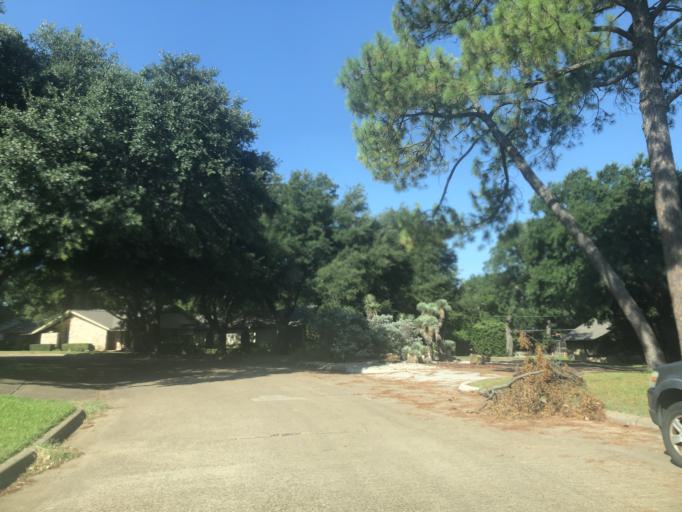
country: US
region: Texas
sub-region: Dallas County
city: Grand Prairie
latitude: 32.7674
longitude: -97.0184
